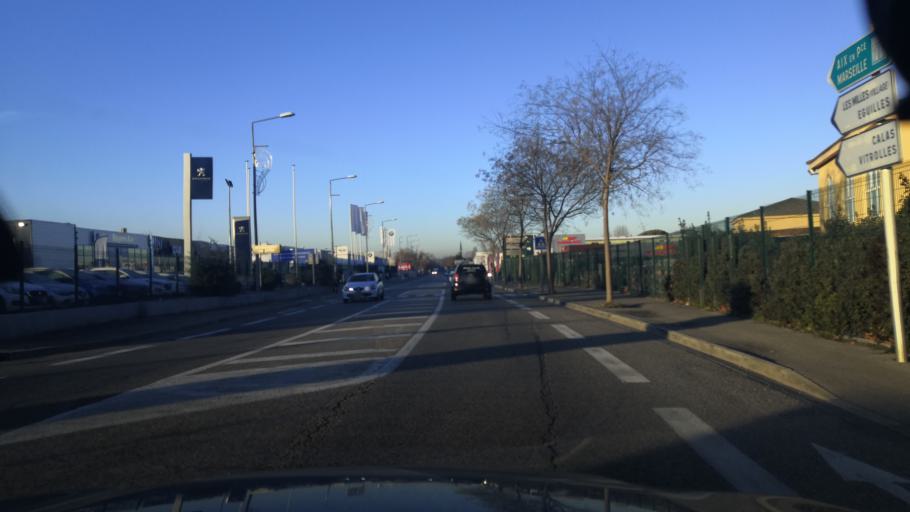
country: FR
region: Provence-Alpes-Cote d'Azur
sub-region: Departement des Bouches-du-Rhone
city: Aix-en-Provence
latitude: 43.5080
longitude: 5.4052
